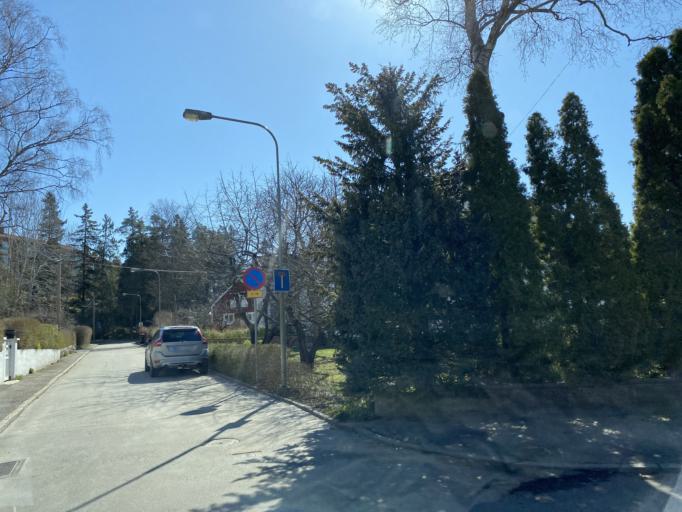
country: SE
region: Stockholm
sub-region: Stockholms Kommun
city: Arsta
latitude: 59.2755
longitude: 18.0624
